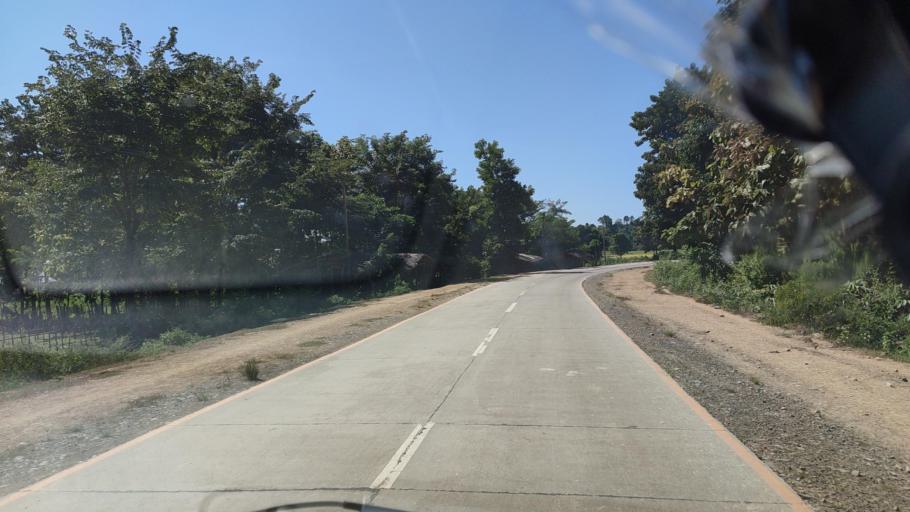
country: MM
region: Rakhine
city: Sittwe
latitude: 20.1300
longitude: 93.4582
